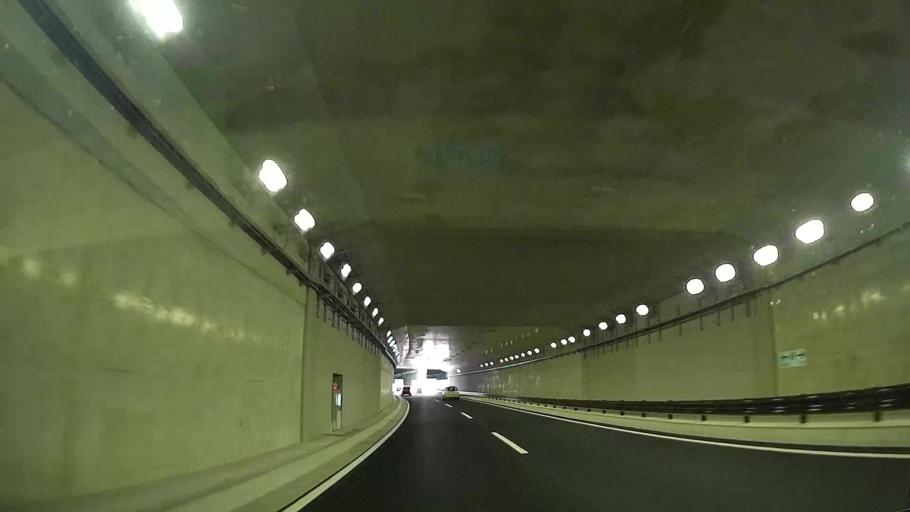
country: JP
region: Chiba
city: Matsudo
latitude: 35.7265
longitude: 139.9183
